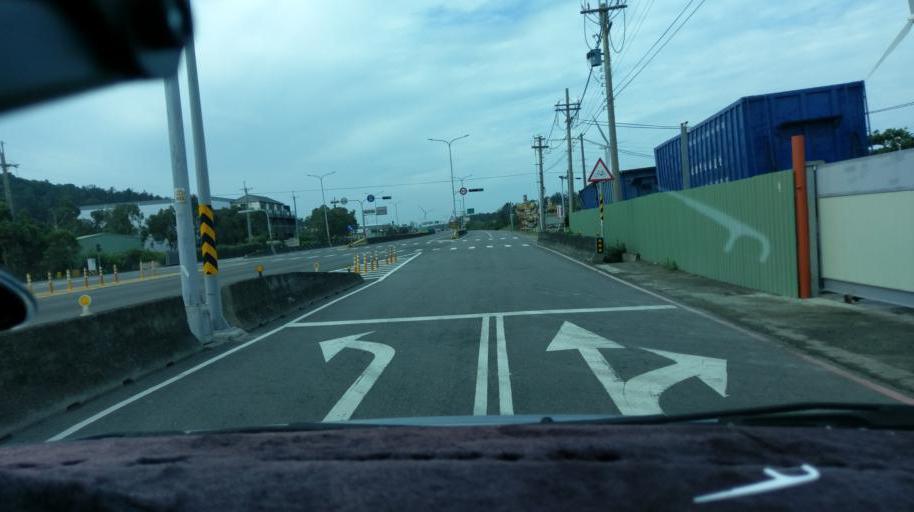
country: TW
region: Taiwan
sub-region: Hsinchu
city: Hsinchu
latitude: 24.7374
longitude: 120.8870
